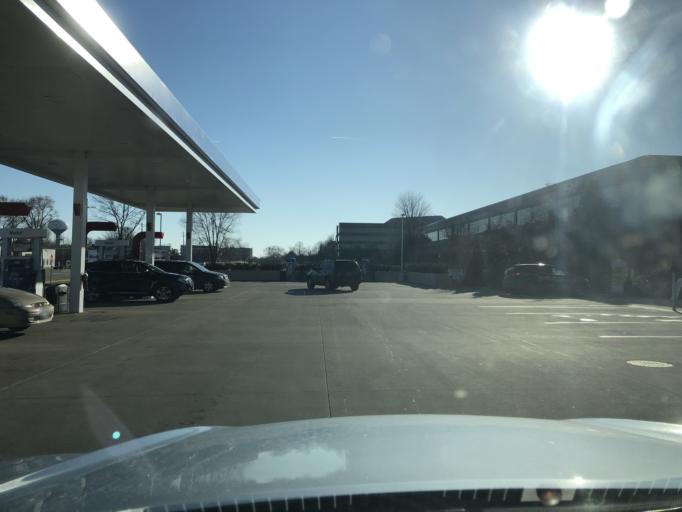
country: US
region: Illinois
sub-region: DuPage County
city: Itasca
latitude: 41.9922
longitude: -88.0036
